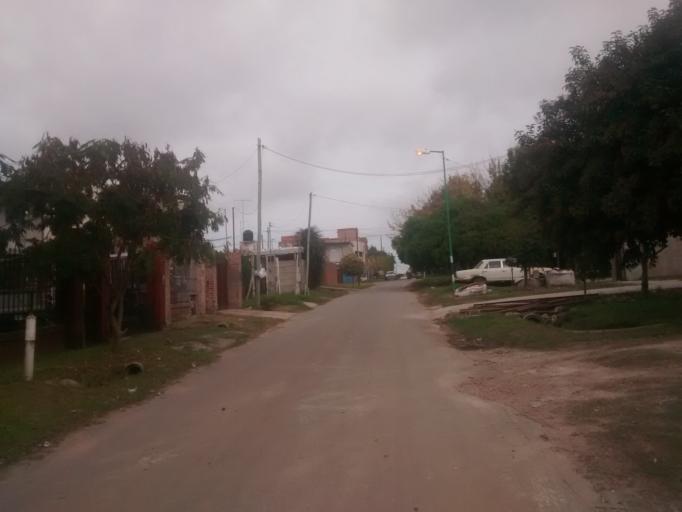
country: AR
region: Buenos Aires
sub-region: Partido de La Plata
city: La Plata
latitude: -34.9350
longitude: -57.9114
